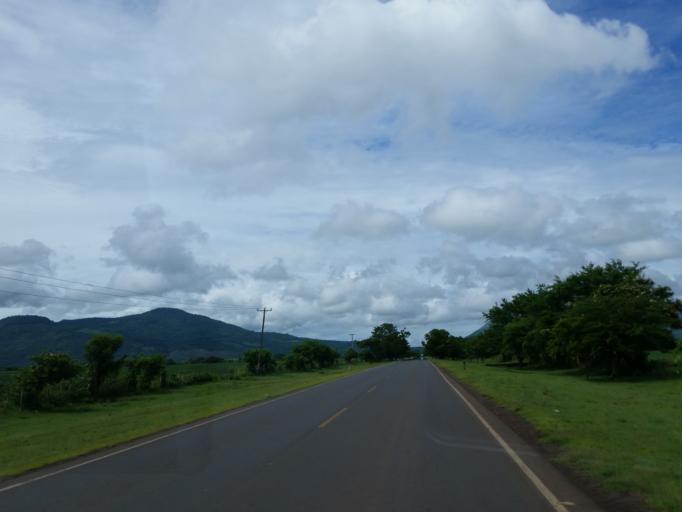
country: NI
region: Leon
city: Larreynaga
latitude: 12.6008
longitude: -86.6889
